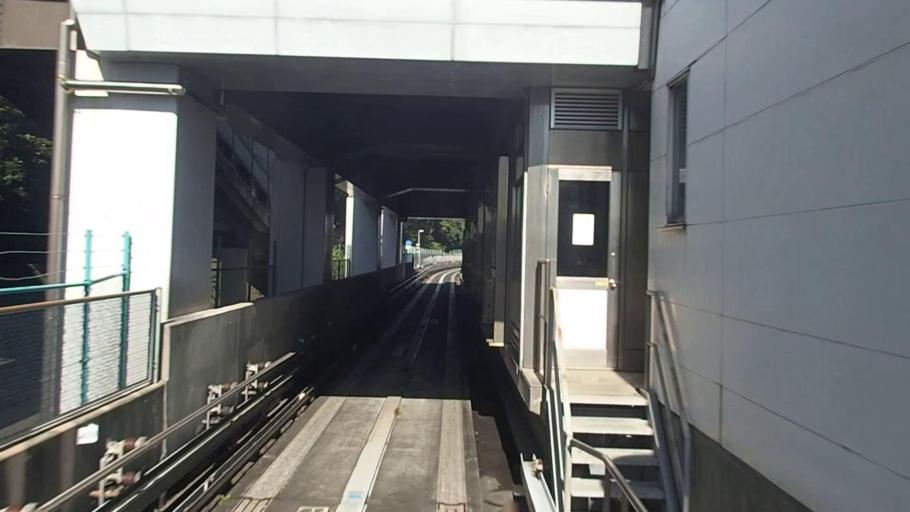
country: JP
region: Kanagawa
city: Yokohama
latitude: 35.3718
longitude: 139.6427
